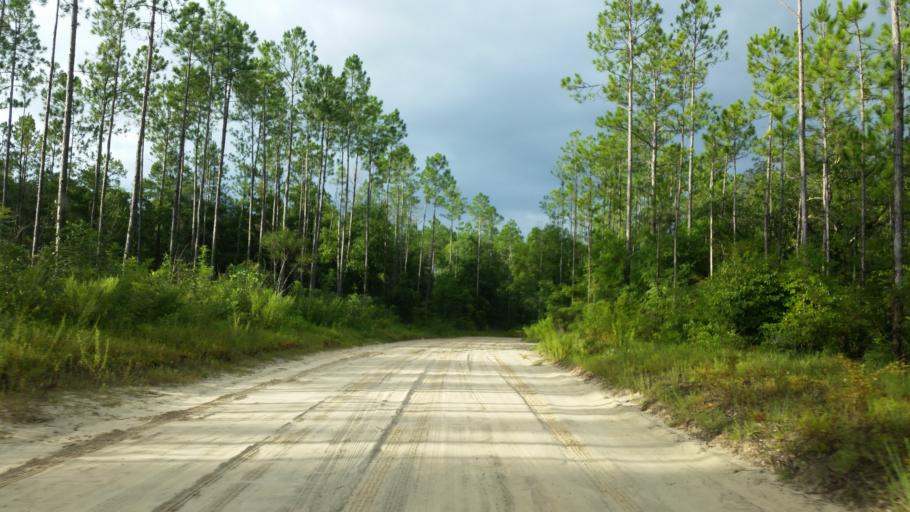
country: US
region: Florida
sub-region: Okaloosa County
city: Crestview
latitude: 30.6626
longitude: -86.7644
